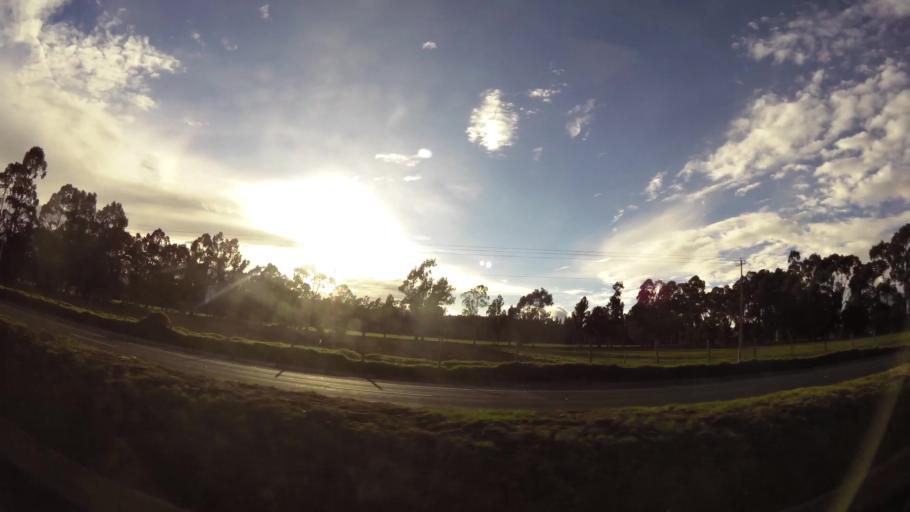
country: EC
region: Cotopaxi
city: Saquisili
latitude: -0.8338
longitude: -78.6189
